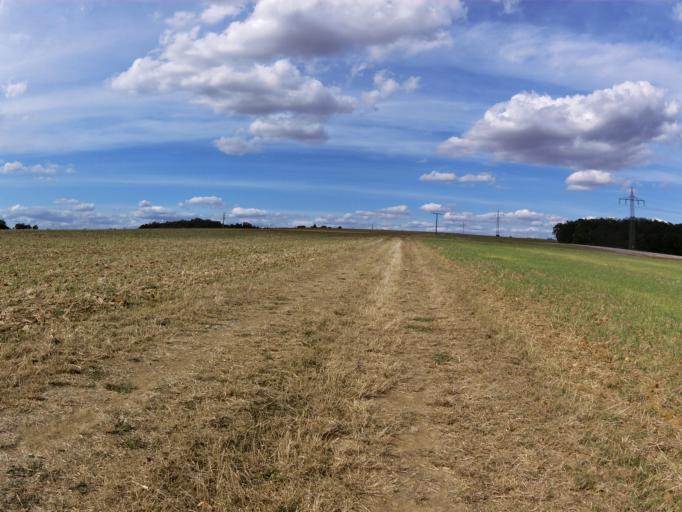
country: DE
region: Bavaria
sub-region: Regierungsbezirk Unterfranken
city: Gadheim
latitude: 49.8580
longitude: 9.9181
